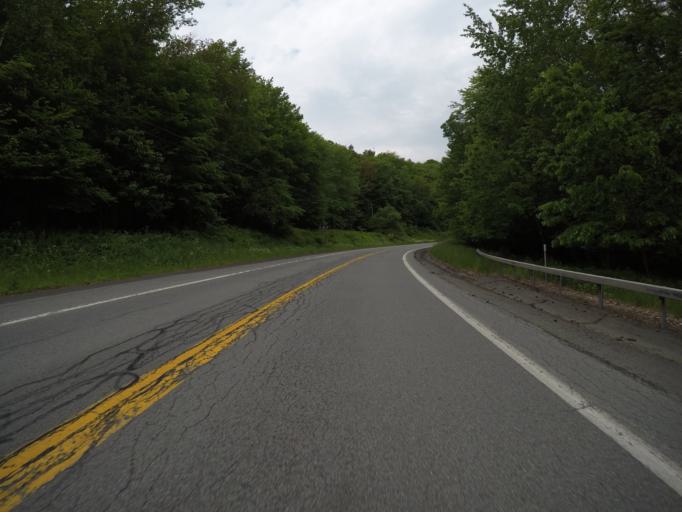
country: US
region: New York
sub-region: Sullivan County
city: Livingston Manor
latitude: 42.0671
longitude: -74.8799
